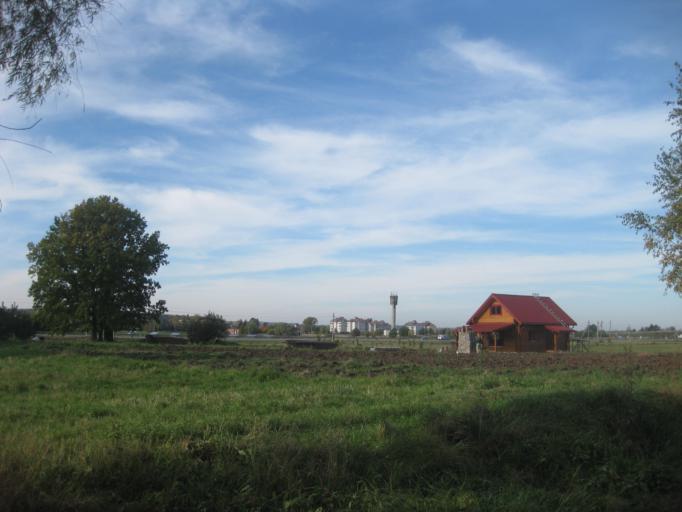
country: LT
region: Kauno apskritis
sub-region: Kauno rajonas
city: Garliava
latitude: 54.8211
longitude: 23.8585
